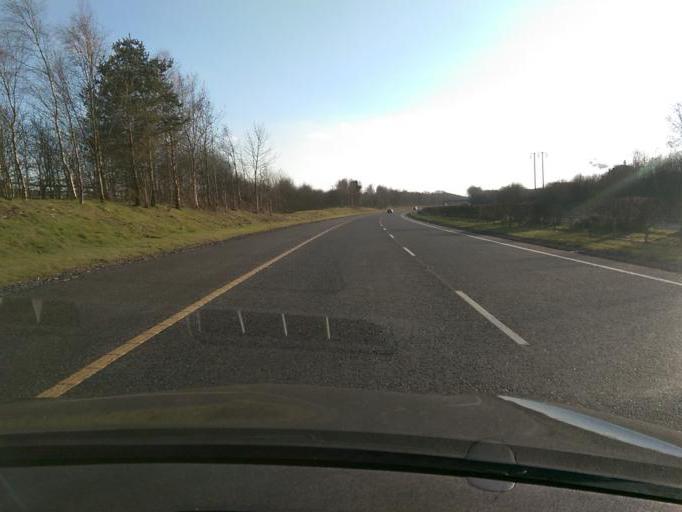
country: IE
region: Leinster
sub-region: Laois
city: Portlaoise
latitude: 53.0359
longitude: -7.2455
